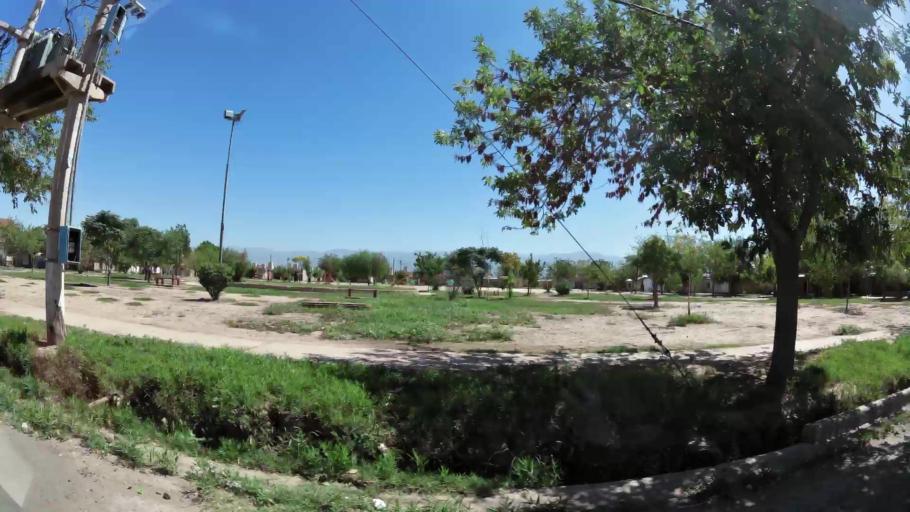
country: AR
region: Mendoza
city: Villa Nueva
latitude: -32.8777
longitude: -68.7871
